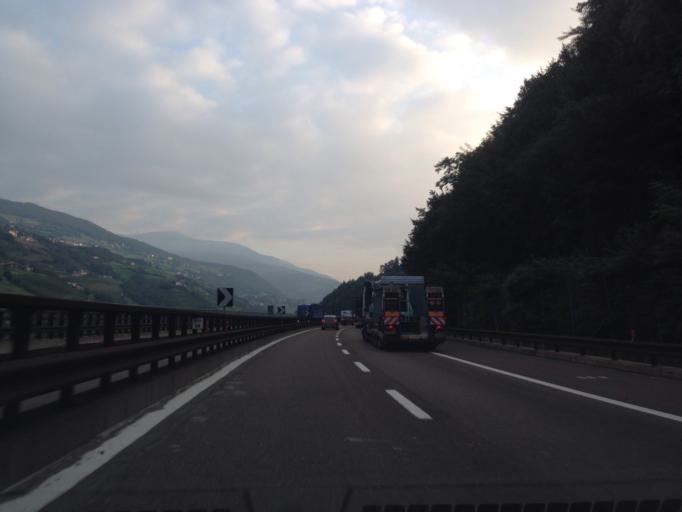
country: IT
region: Trentino-Alto Adige
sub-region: Bolzano
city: Ponte Gardena
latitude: 46.6110
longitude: 11.5370
